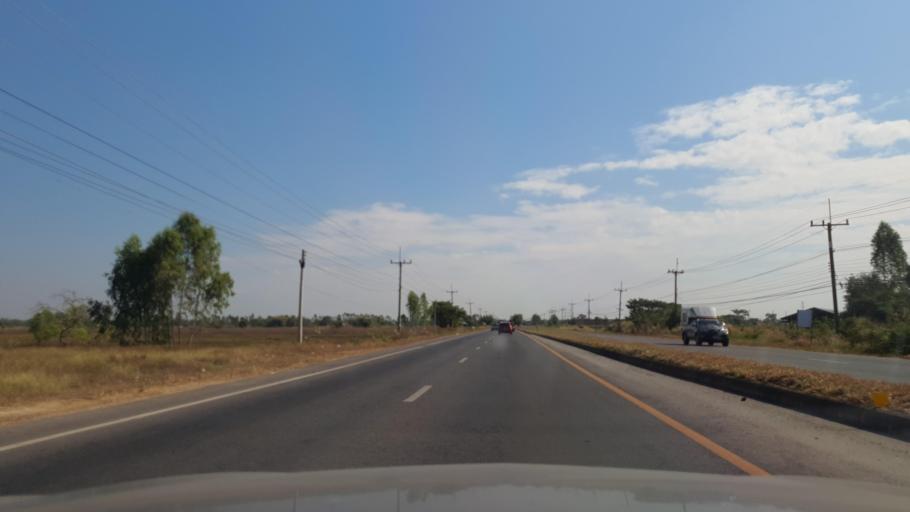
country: TH
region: Maha Sarakham
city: Chiang Yuen
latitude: 16.3748
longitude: 103.1602
